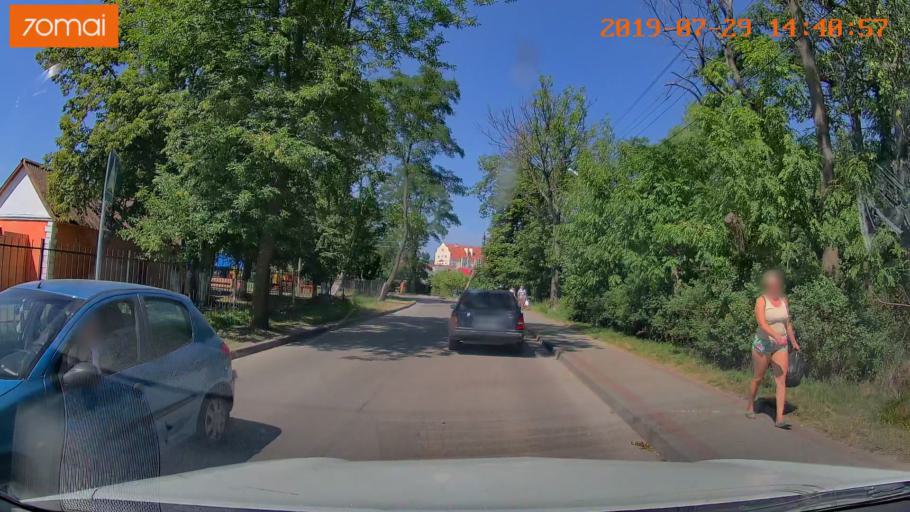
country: RU
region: Kaliningrad
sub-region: Gorod Kaliningrad
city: Baltiysk
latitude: 54.6563
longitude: 19.9005
